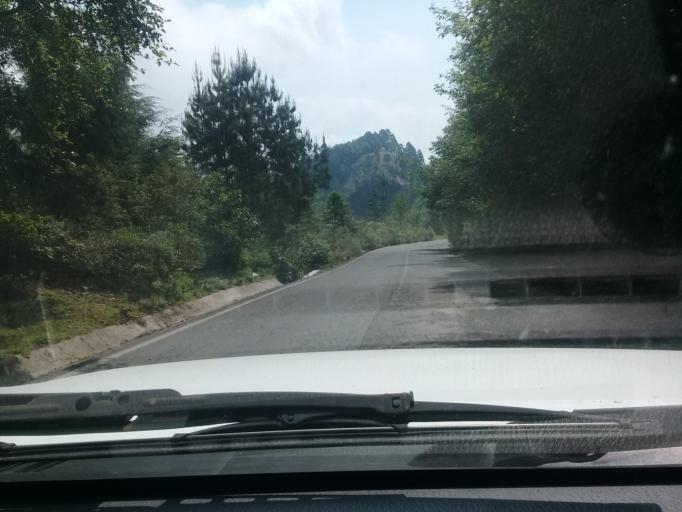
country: MX
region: Veracruz
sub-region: Mariano Escobedo
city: San Isidro el Berro
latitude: 18.9466
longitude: -97.2184
